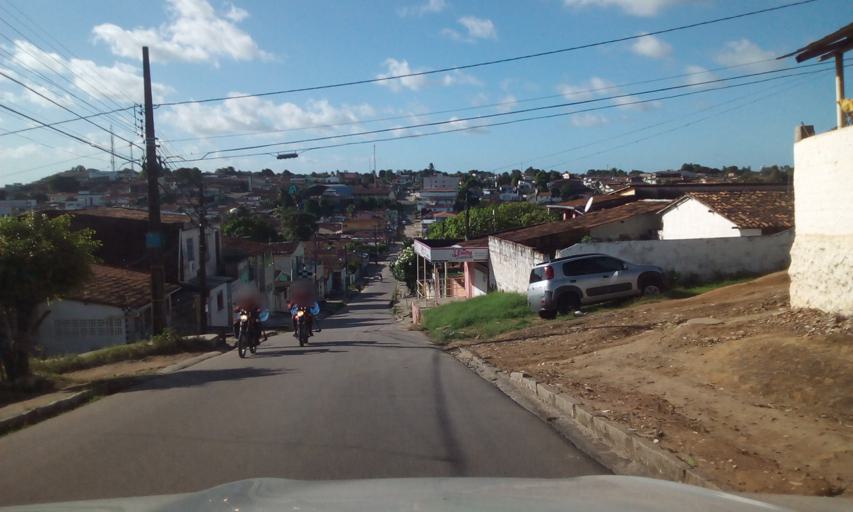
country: BR
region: Paraiba
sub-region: Bayeux
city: Bayeux
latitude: -7.1570
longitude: -34.8928
